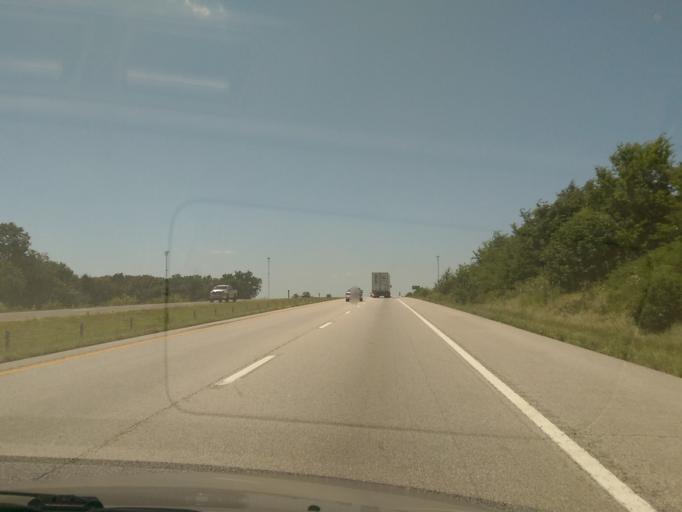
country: US
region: Missouri
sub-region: Saline County
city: Marshall
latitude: 38.9489
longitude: -93.0240
